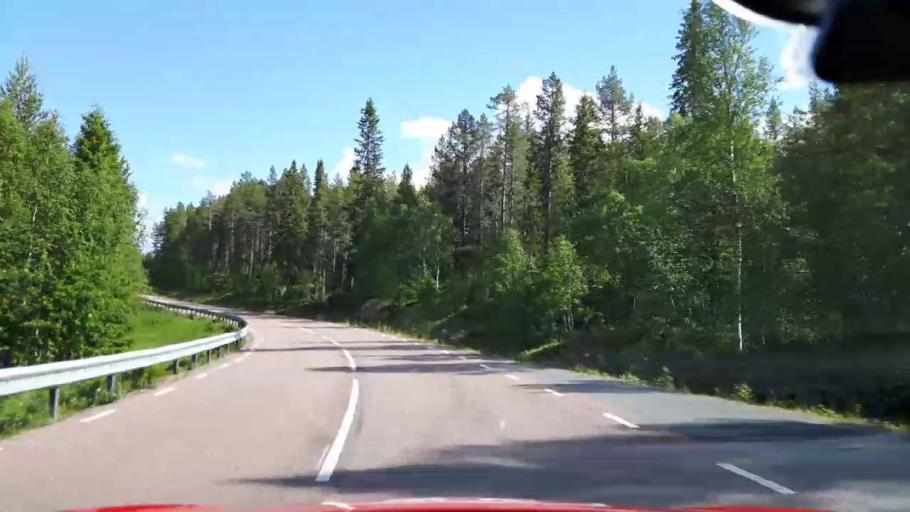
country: SE
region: Jaemtland
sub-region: Krokoms Kommun
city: Valla
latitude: 64.0091
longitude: 14.2325
